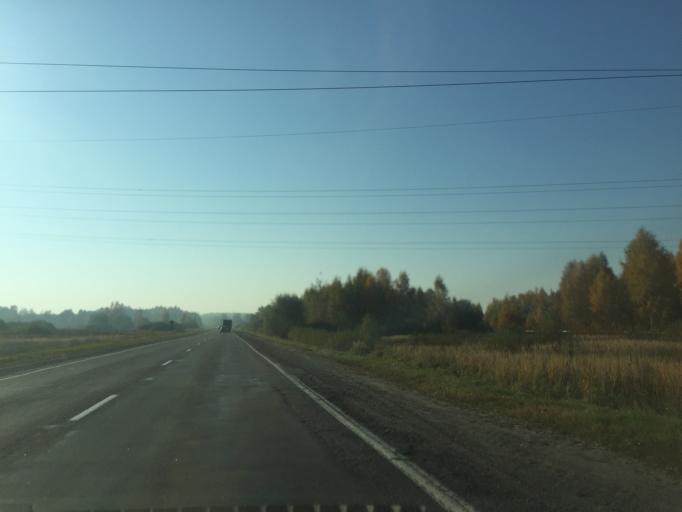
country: BY
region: Gomel
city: Kastsyukowka
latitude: 52.4485
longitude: 30.8247
